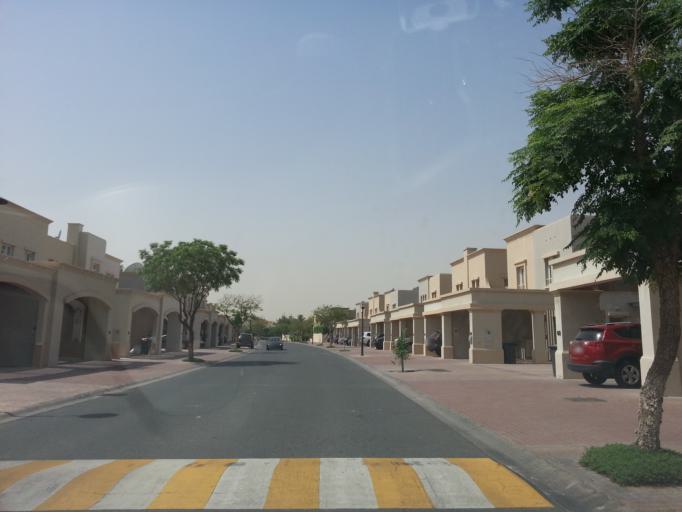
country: AE
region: Dubai
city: Dubai
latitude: 25.0520
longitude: 55.1735
